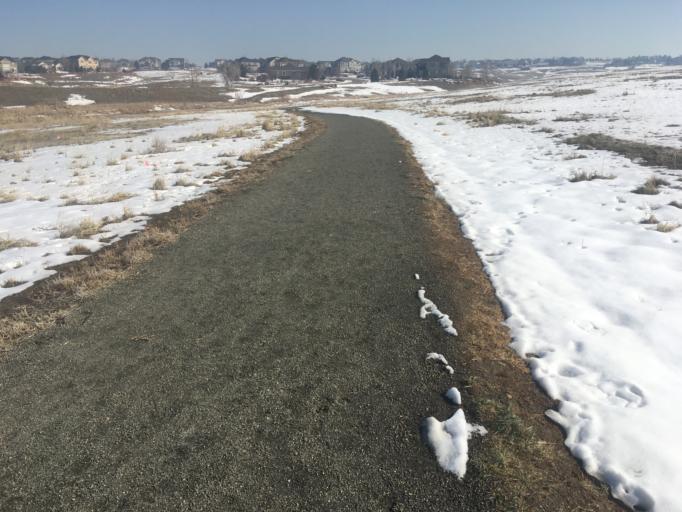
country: US
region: Colorado
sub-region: Boulder County
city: Lafayette
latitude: 39.9716
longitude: -105.0570
